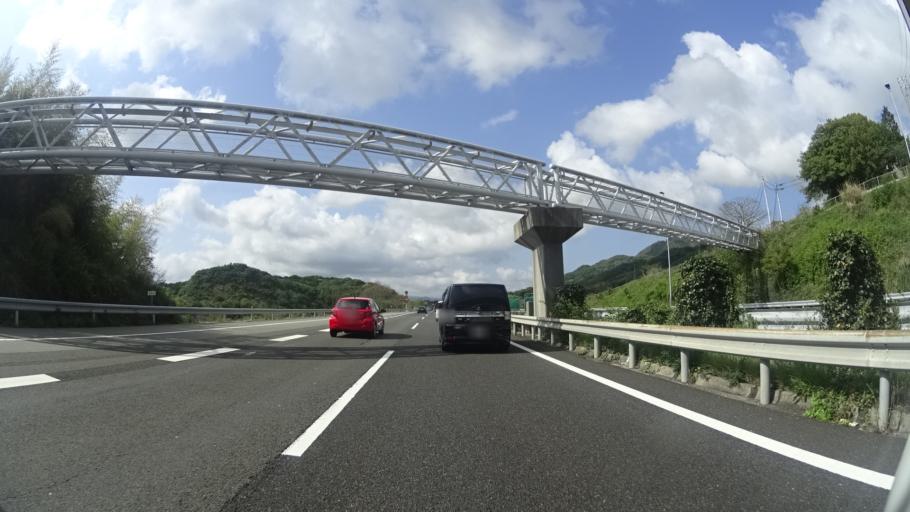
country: JP
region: Hyogo
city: Sumoto
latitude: 34.3719
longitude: 134.8601
